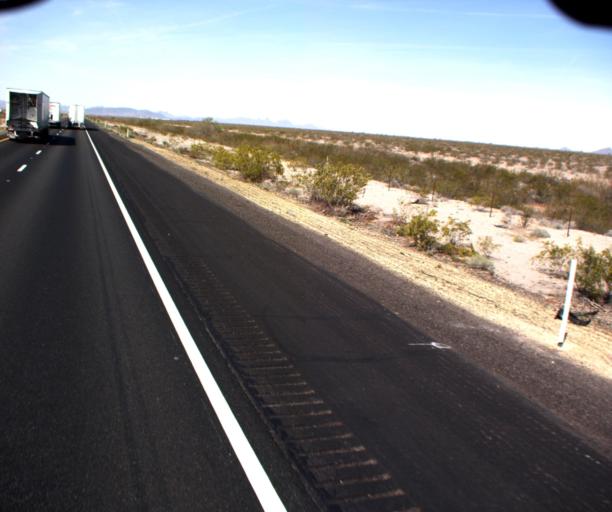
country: US
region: Arizona
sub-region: La Paz County
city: Salome
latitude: 33.6180
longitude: -113.6781
